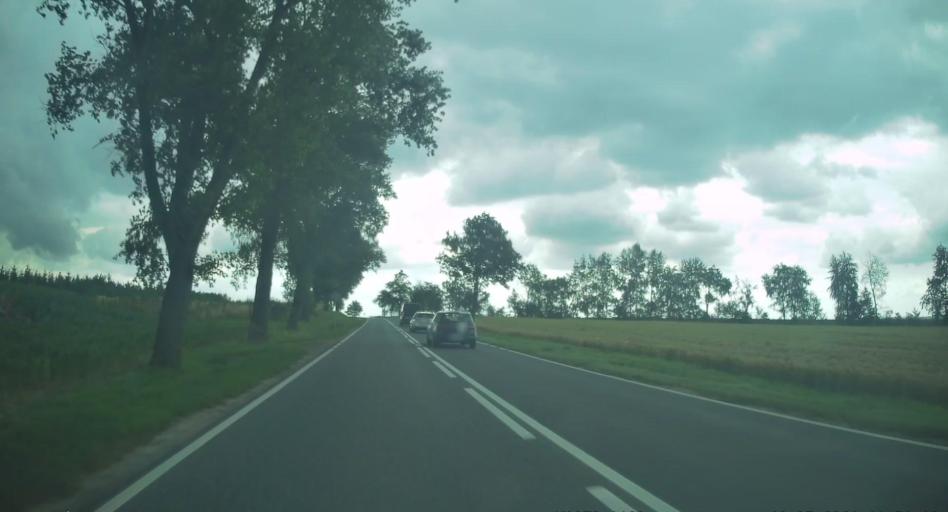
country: PL
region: Opole Voivodeship
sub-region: Powiat nyski
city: Glucholazy
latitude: 50.4226
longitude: 17.4527
